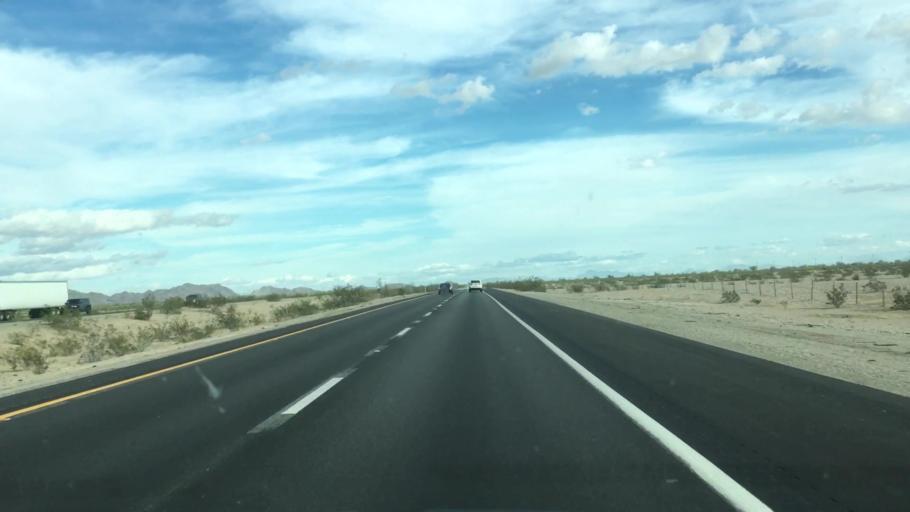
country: US
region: California
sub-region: Riverside County
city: Mesa Verde
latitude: 33.6089
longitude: -114.8631
